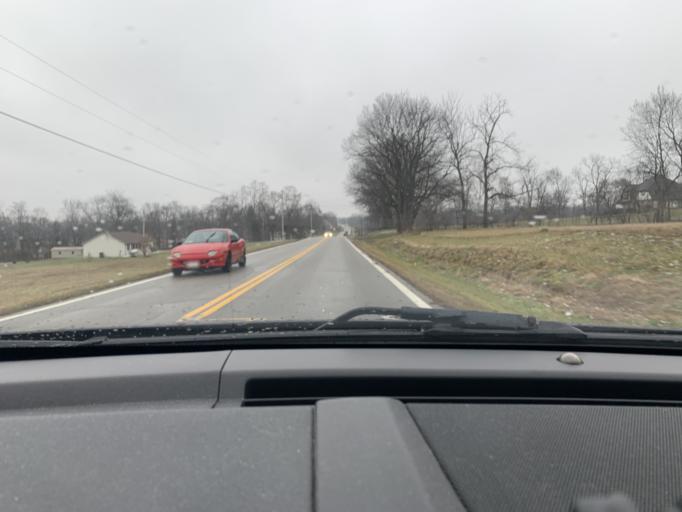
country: US
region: Ohio
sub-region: Ross County
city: Kingston
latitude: 39.4295
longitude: -82.9291
